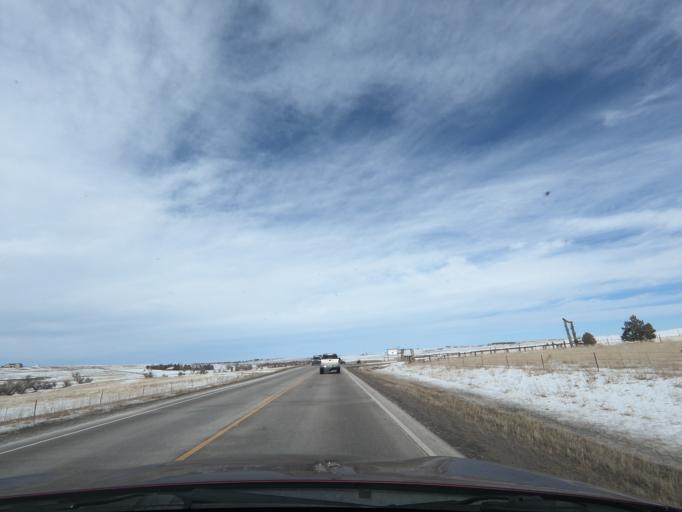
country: US
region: Colorado
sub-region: El Paso County
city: Woodmoor
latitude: 39.2125
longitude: -104.7104
